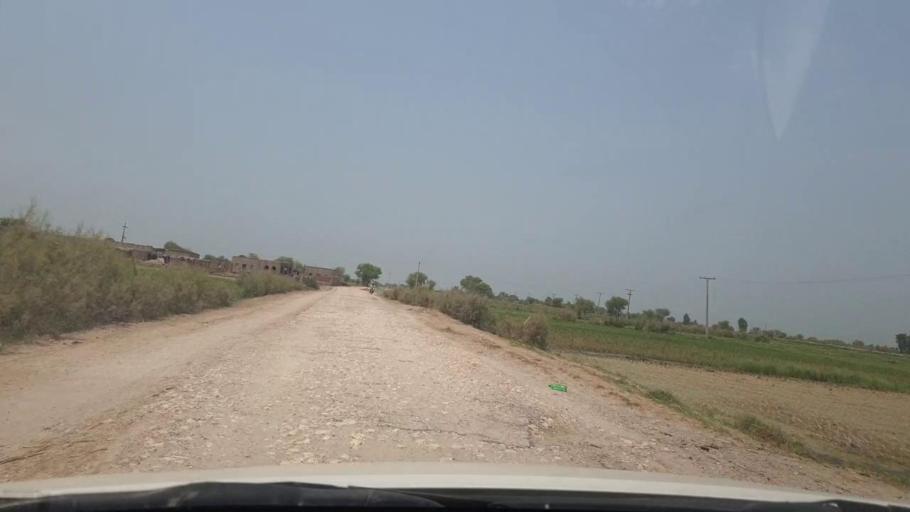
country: PK
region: Sindh
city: Rustam jo Goth
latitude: 28.0354
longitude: 68.7563
